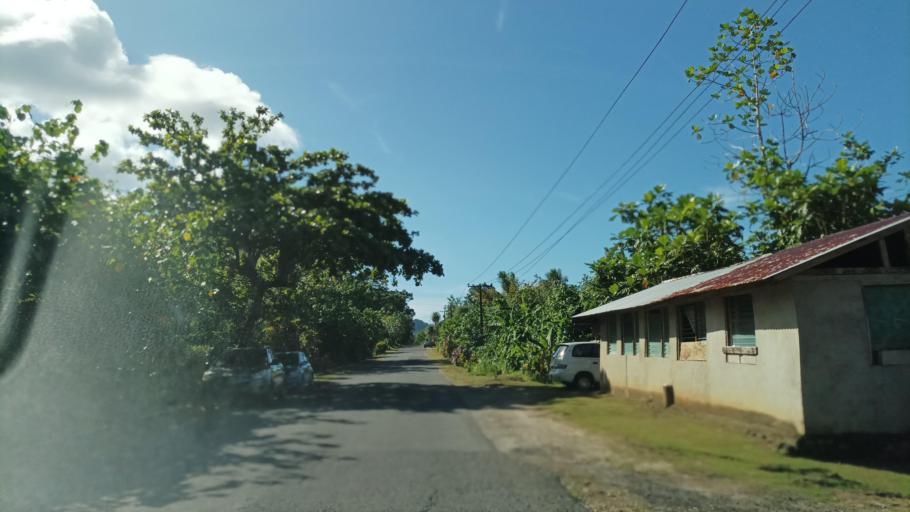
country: FM
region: Pohnpei
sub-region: Madolenihm Municipality
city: Madolenihm Municipality Government
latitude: 6.9192
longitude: 158.2889
